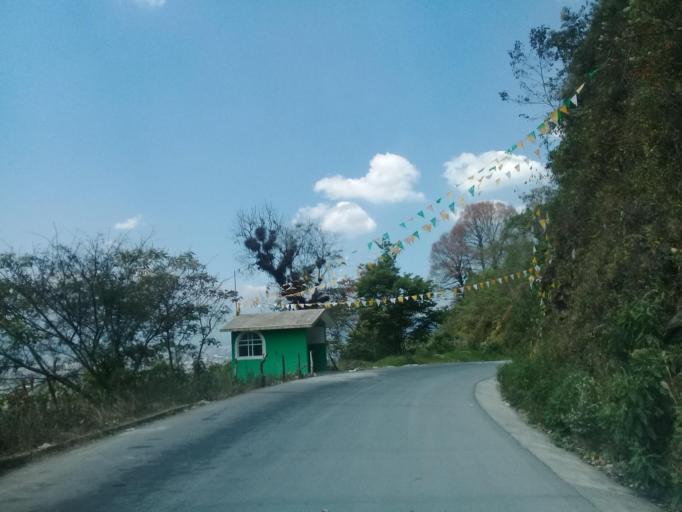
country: MX
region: Veracruz
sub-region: Tlilapan
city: Tonalixco
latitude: 18.8084
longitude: -97.0606
